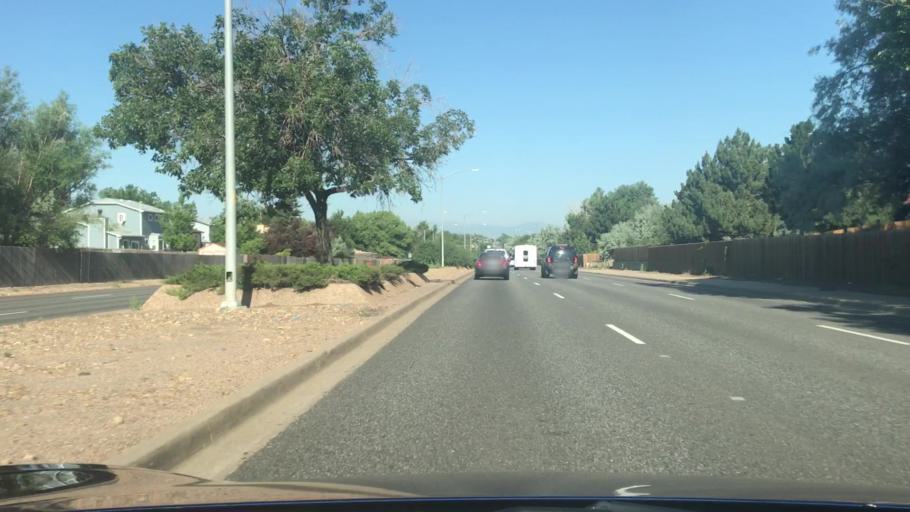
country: US
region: Colorado
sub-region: Arapahoe County
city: Dove Valley
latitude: 39.6531
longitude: -104.7878
